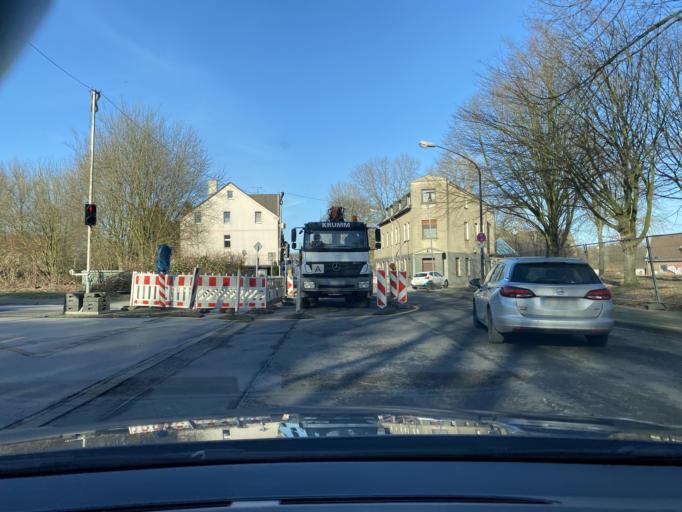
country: DE
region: North Rhine-Westphalia
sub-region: Regierungsbezirk Dusseldorf
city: Essen
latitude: 51.4955
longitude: 7.0545
